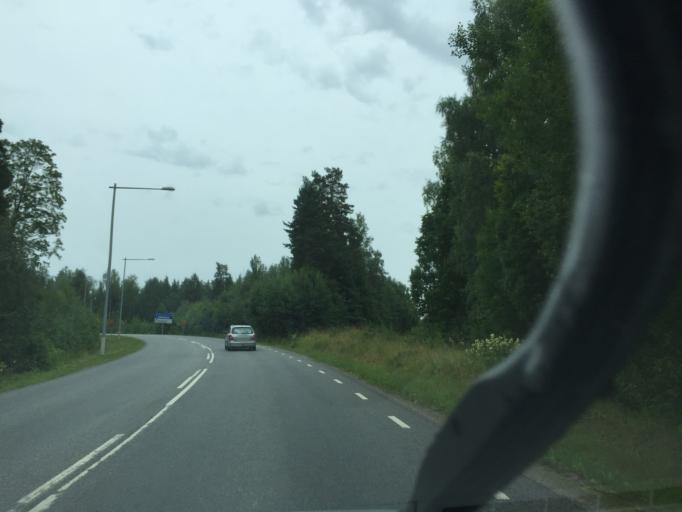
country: SE
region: OErebro
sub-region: Orebro Kommun
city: Orebro
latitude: 59.2461
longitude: 15.1984
